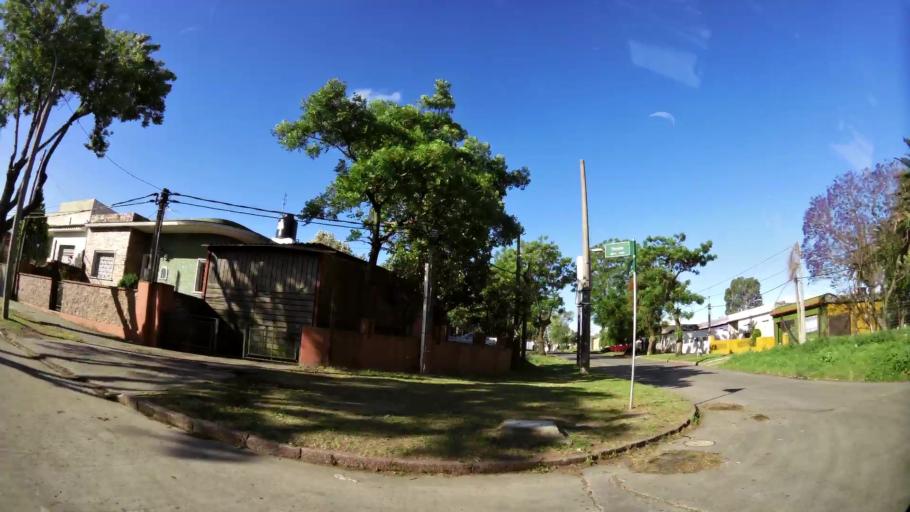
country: UY
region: Montevideo
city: Montevideo
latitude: -34.8436
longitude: -56.2368
